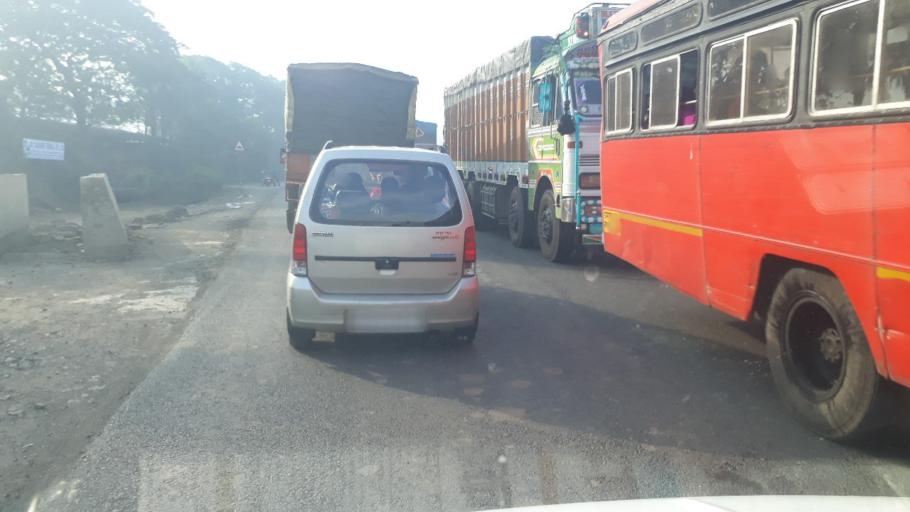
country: IN
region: Maharashtra
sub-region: Raigarh
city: Kalundri
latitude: 18.9230
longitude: 73.1256
